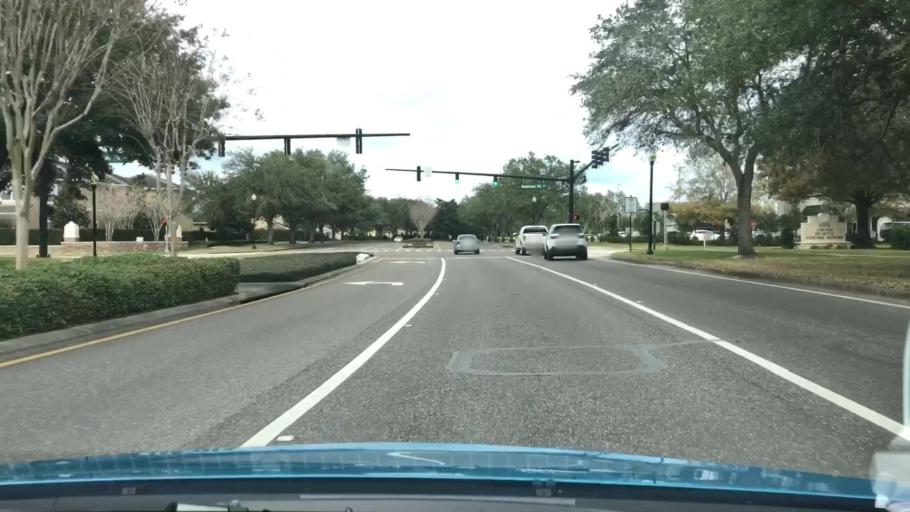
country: US
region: Florida
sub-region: Seminole County
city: Heathrow
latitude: 28.7802
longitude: -81.3574
